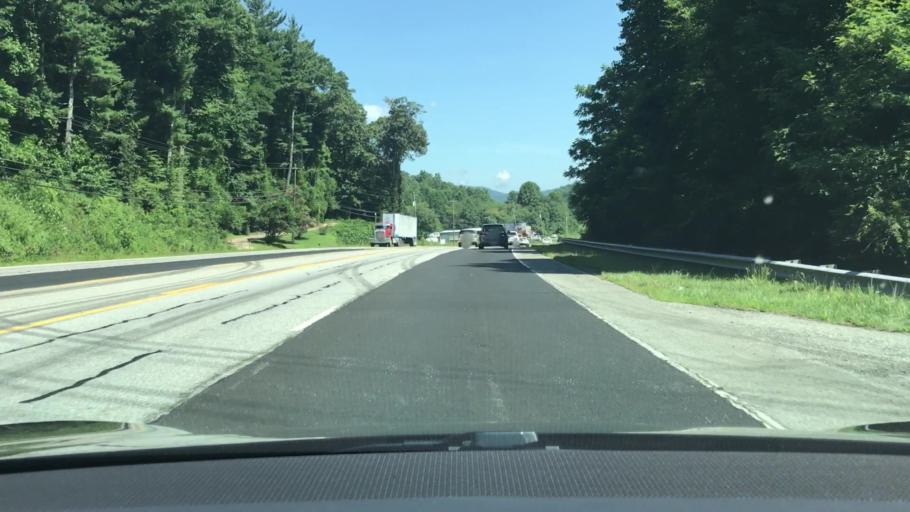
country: US
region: Georgia
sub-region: Rabun County
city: Mountain City
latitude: 34.9298
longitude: -83.3887
